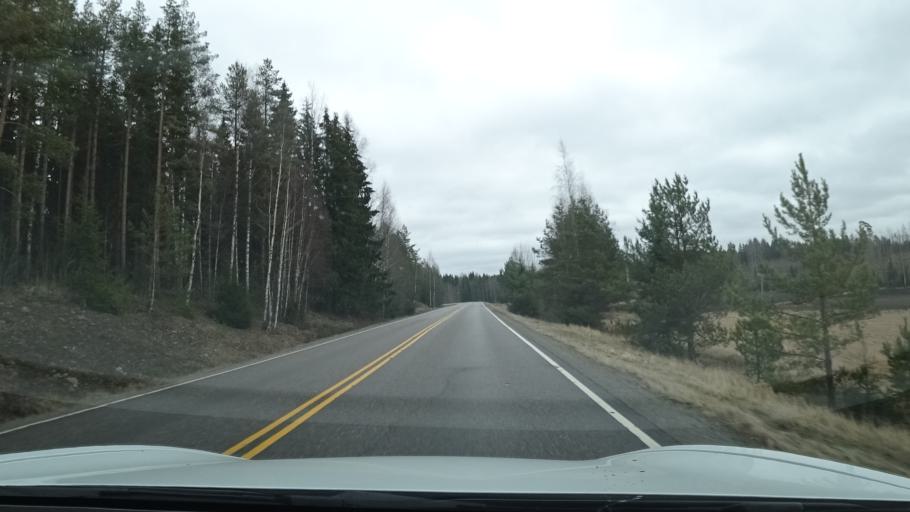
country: FI
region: Uusimaa
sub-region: Helsinki
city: Pornainen
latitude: 60.4931
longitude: 25.4740
